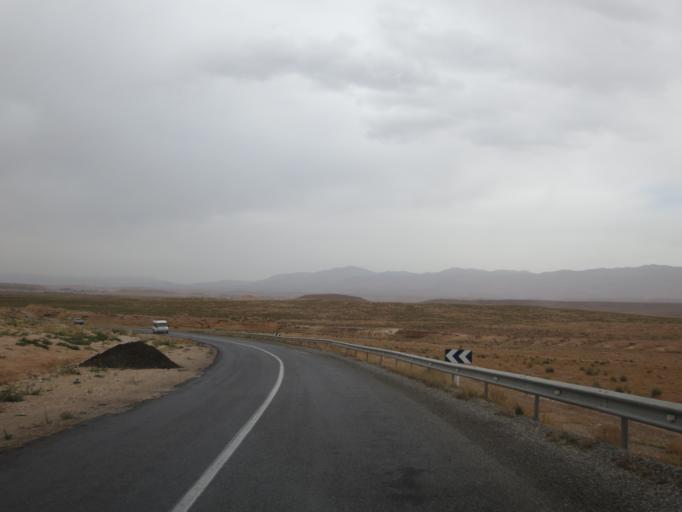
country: MA
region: Meknes-Tafilalet
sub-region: Khenifra
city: Midelt
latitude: 32.6980
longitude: -4.8433
